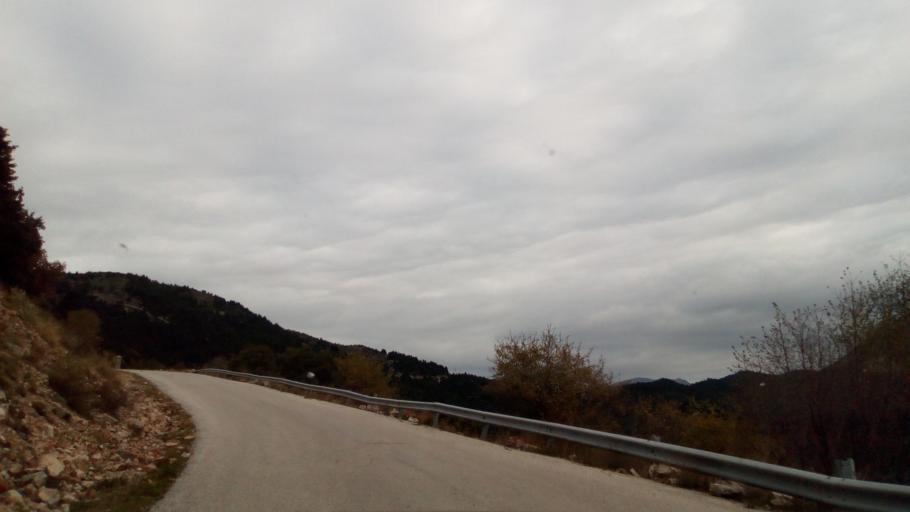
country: GR
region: West Greece
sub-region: Nomos Aitolias kai Akarnanias
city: Thermo
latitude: 38.6134
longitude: 21.8193
